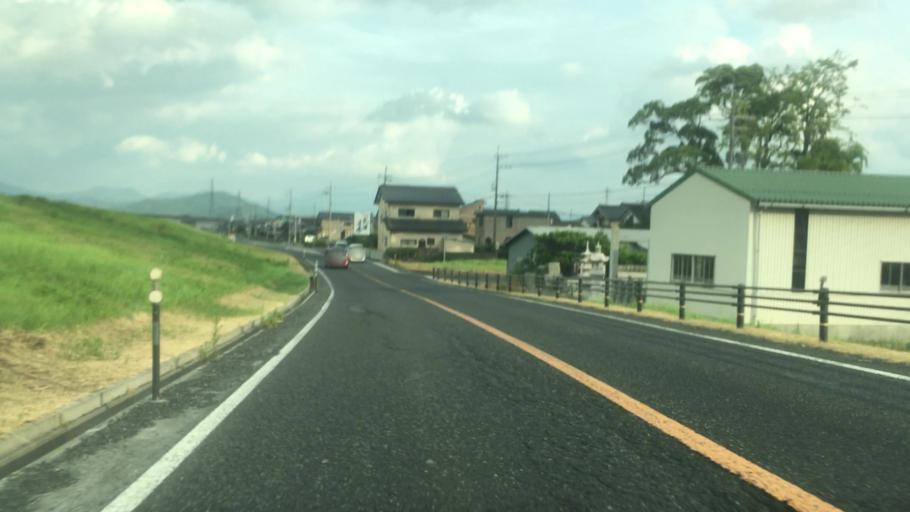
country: JP
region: Hyogo
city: Toyooka
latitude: 35.5601
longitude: 134.8148
